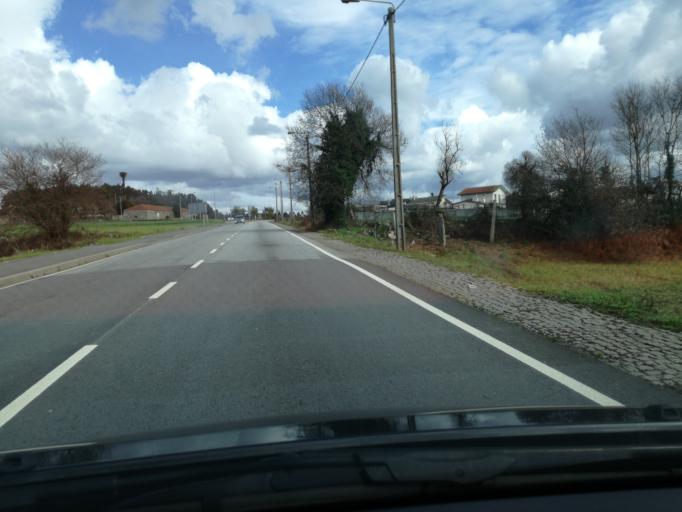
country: PT
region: Porto
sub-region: Maia
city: Nogueira
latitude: 41.2532
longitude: -8.5854
